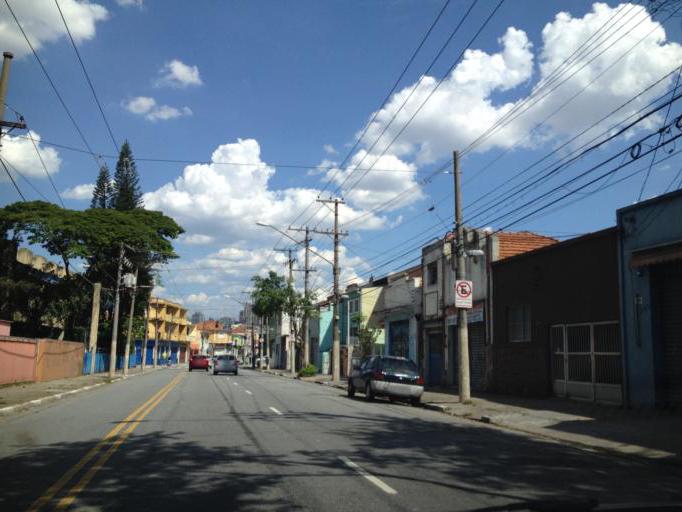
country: BR
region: Sao Paulo
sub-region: Sao Paulo
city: Sao Paulo
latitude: -23.5548
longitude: -46.5928
